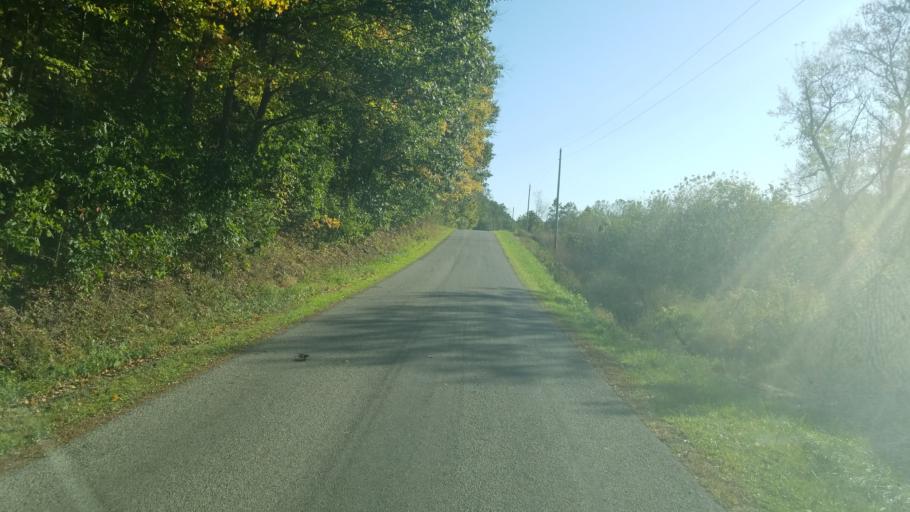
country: US
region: Ohio
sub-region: Wayne County
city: Wooster
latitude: 40.8989
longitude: -82.0079
